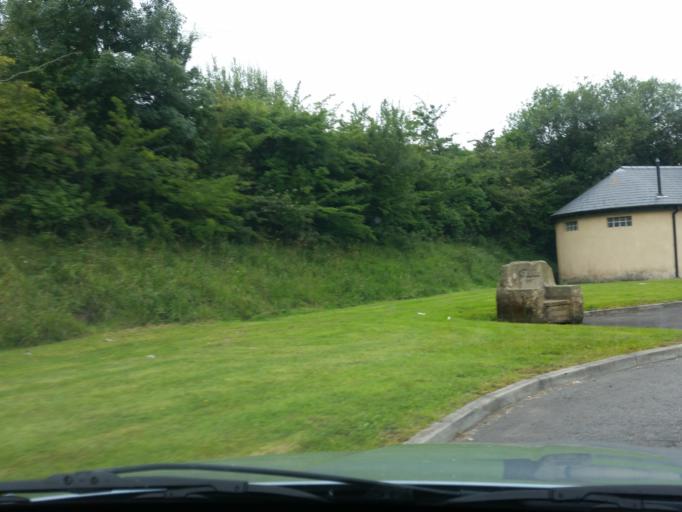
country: GB
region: Northern Ireland
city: Lisnaskea
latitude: 54.2003
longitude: -7.4924
